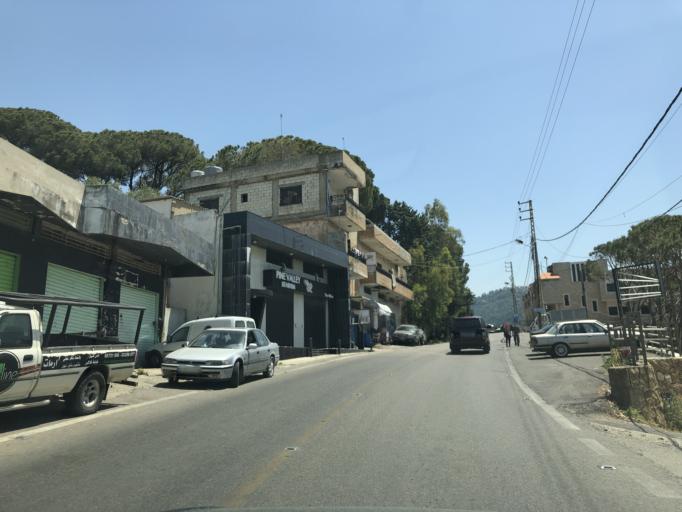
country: LB
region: Mont-Liban
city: Beit ed Dine
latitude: 33.6878
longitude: 35.5204
